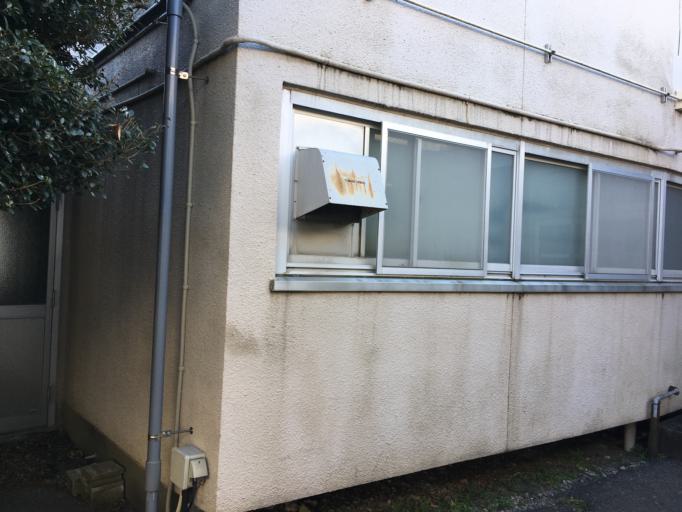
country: JP
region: Tochigi
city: Tanuma
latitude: 36.3568
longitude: 139.5553
